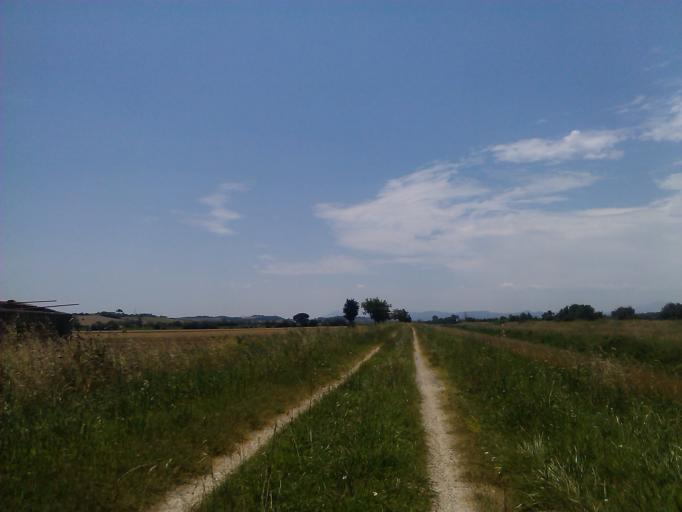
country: IT
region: Tuscany
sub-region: Province of Arezzo
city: Cesa
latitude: 43.2883
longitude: 11.8415
